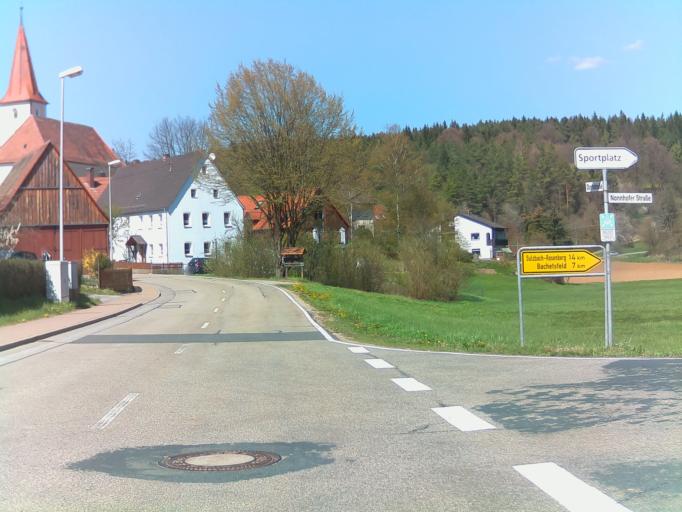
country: DE
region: Bavaria
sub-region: Upper Palatinate
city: Weigendorf
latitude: 49.4554
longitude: 11.5997
